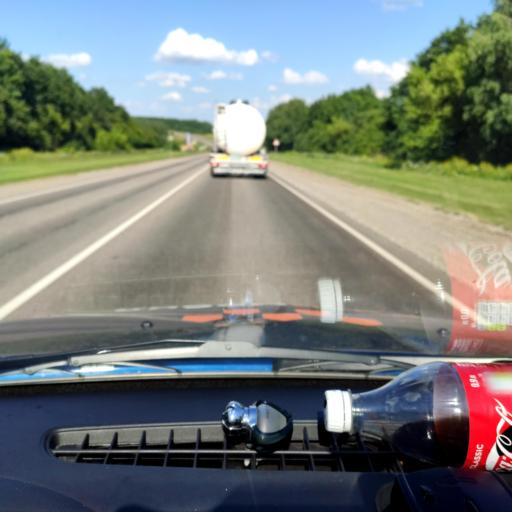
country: RU
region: Lipetsk
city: Kazaki
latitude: 52.5867
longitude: 38.2266
